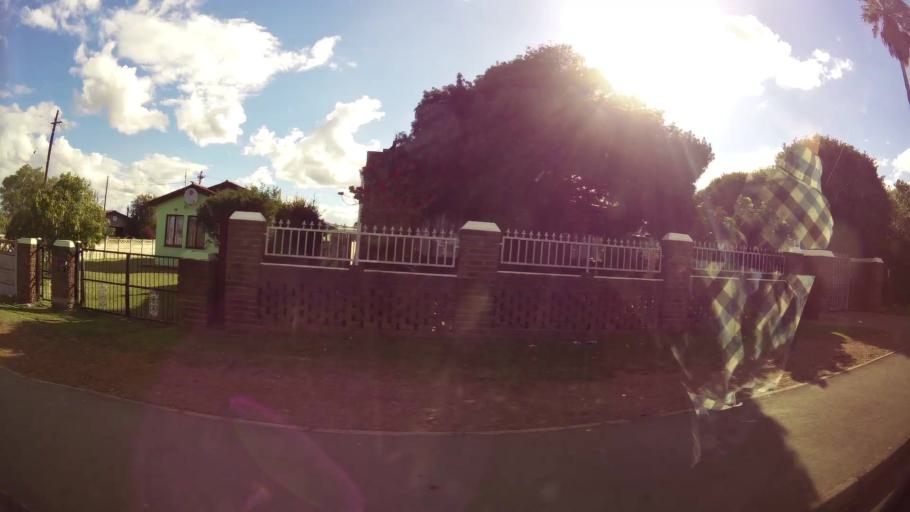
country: ZA
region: Western Cape
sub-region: Overberg District Municipality
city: Swellendam
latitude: -34.0353
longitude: 20.4437
